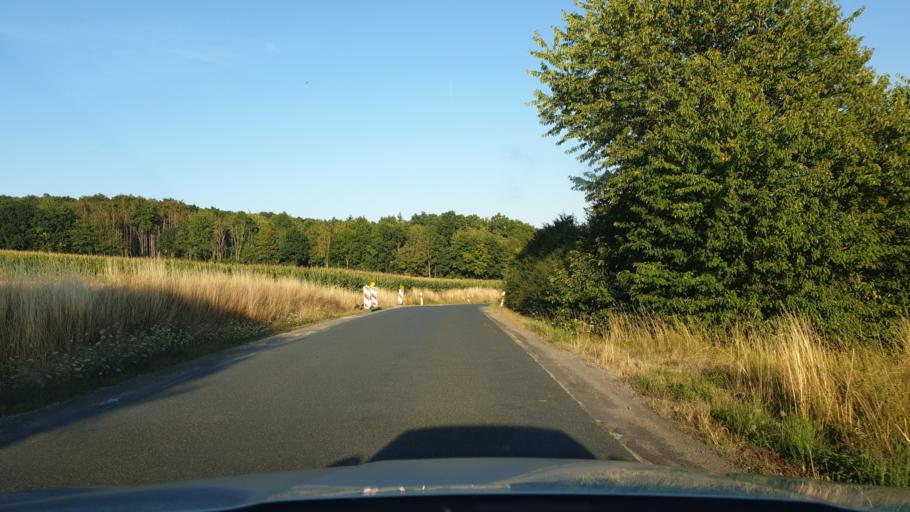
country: DE
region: Lower Saxony
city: Apelern
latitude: 52.2871
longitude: 9.3097
